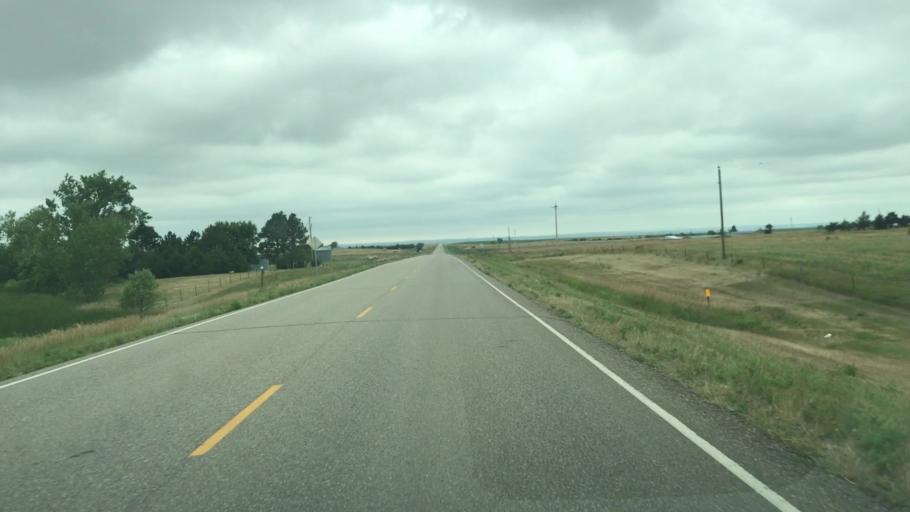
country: US
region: South Dakota
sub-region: Jackson County
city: Kadoka
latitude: 43.8300
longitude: -101.5225
